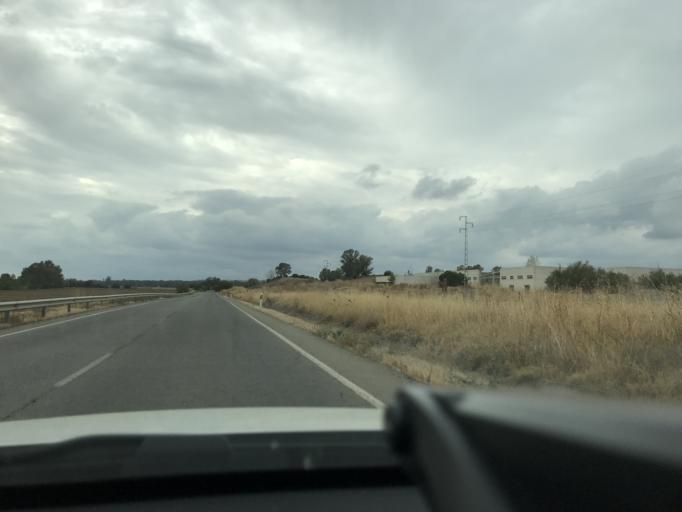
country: ES
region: Andalusia
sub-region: Provincia de Sevilla
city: Villanueva del Rio y Minas
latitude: 37.6353
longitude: -5.7178
